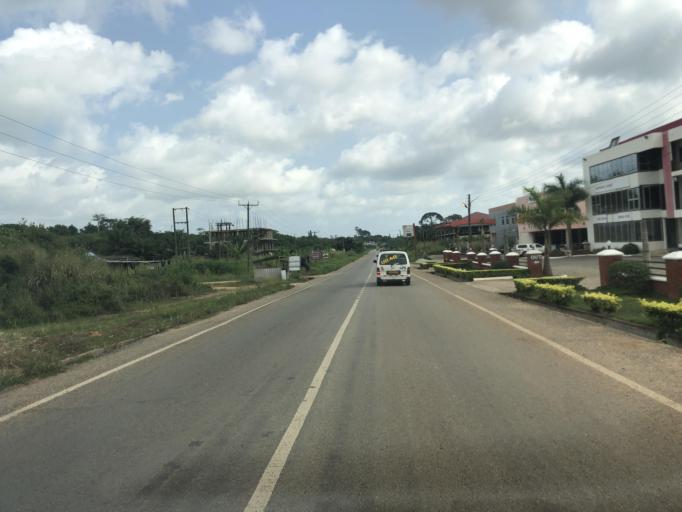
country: GH
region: Central
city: Cape Coast
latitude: 5.1868
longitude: -1.3118
